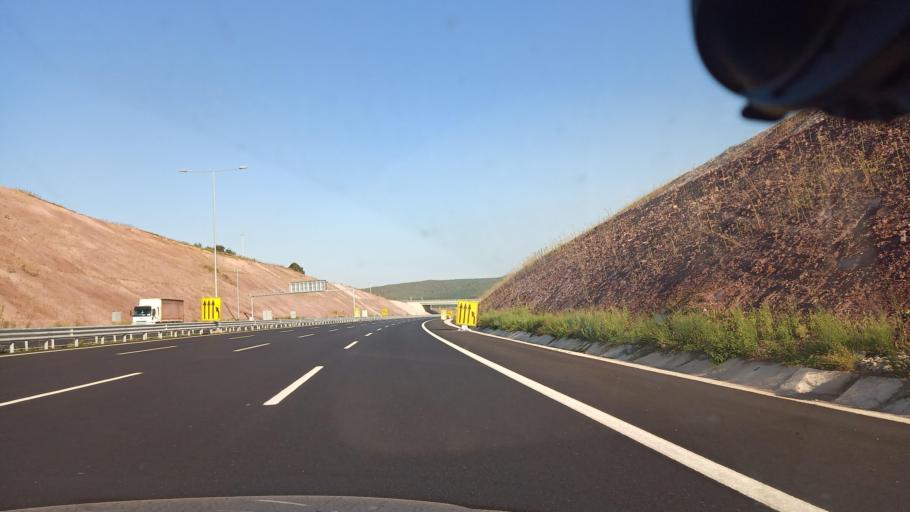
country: TR
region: Sakarya
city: Adapazari
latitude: 40.8391
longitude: 30.3772
